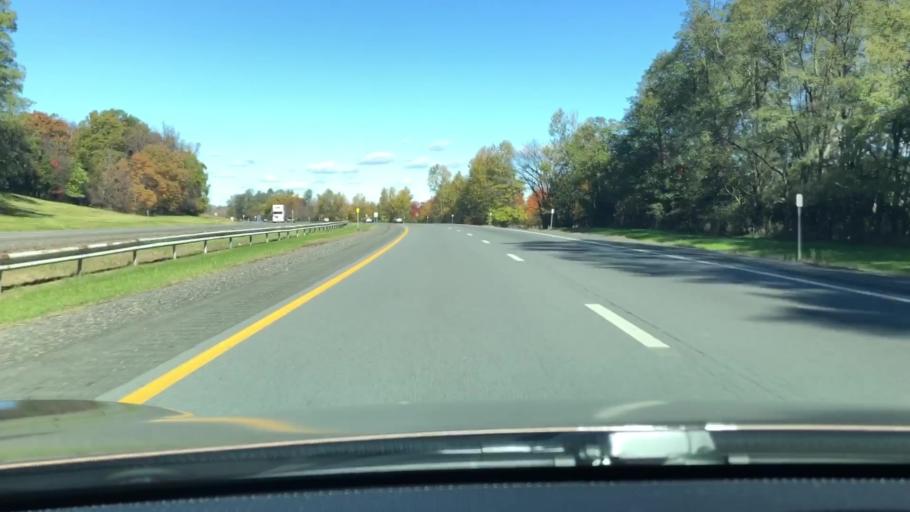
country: US
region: New York
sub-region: Orange County
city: Firthcliffe
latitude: 41.4162
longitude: -74.0700
